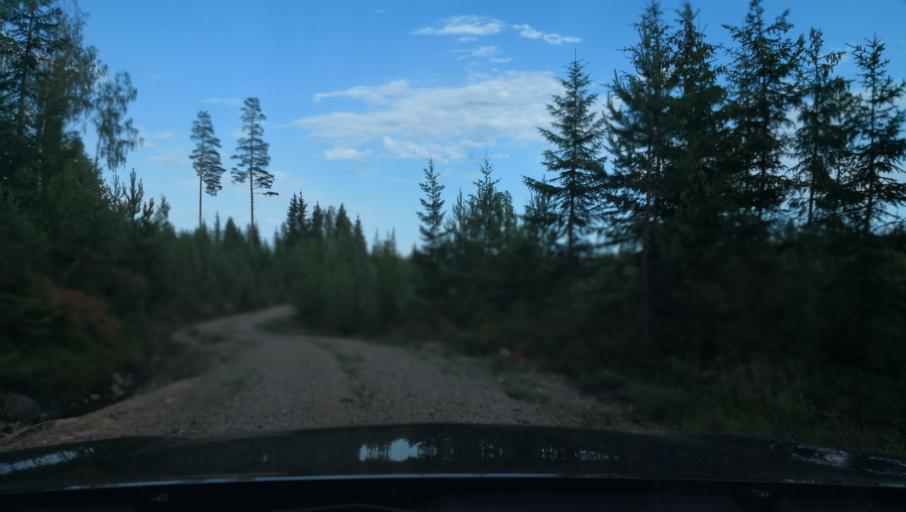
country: SE
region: Dalarna
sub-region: Smedjebackens Kommun
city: Smedjebacken
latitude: 60.0607
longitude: 15.3113
